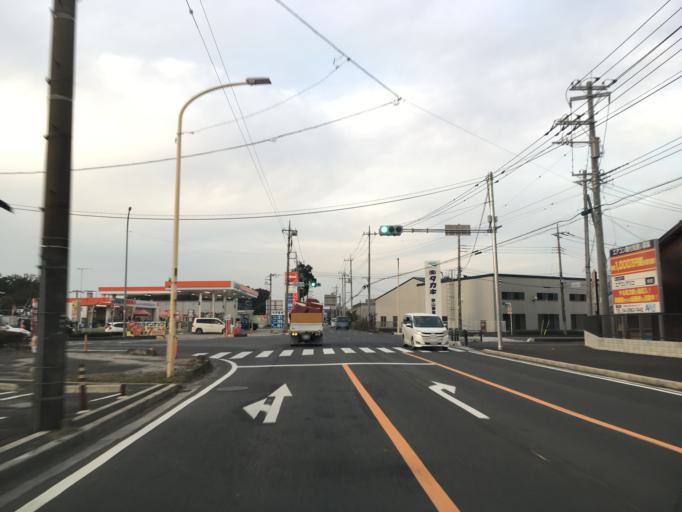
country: JP
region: Saitama
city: Sayama
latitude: 35.8683
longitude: 139.3801
